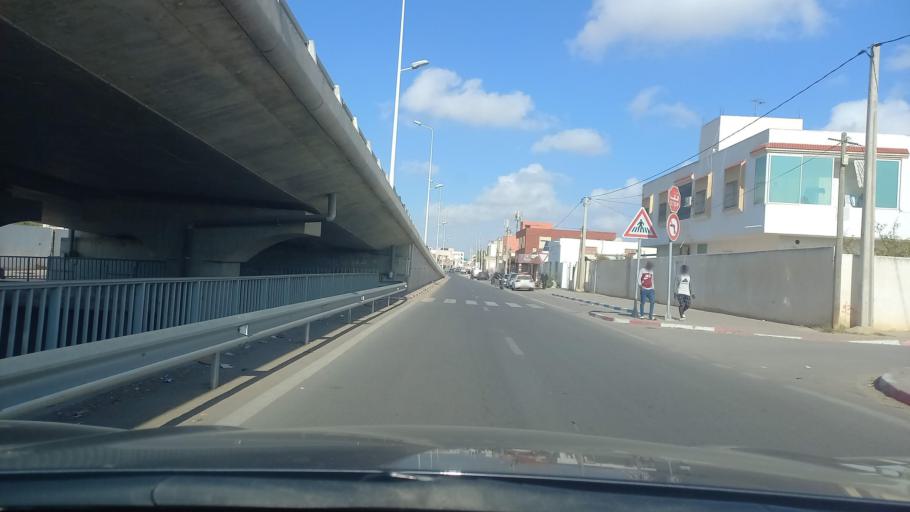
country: TN
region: Safaqis
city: Sfax
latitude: 34.7343
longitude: 10.7245
